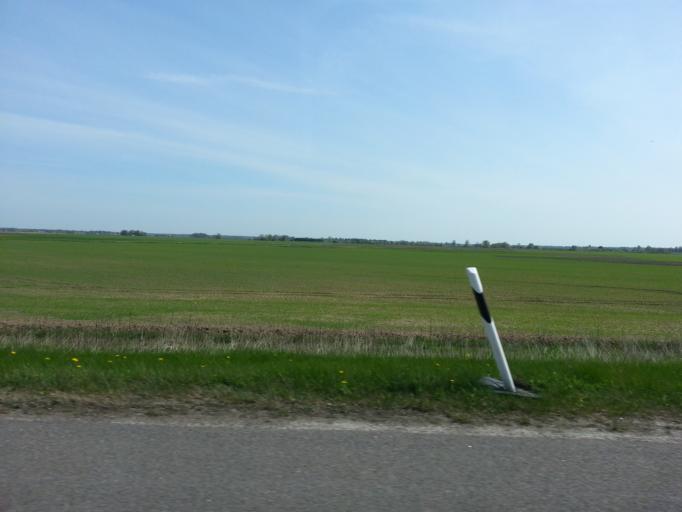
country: LT
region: Panevezys
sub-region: Panevezys City
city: Panevezys
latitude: 55.5976
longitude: 24.4459
